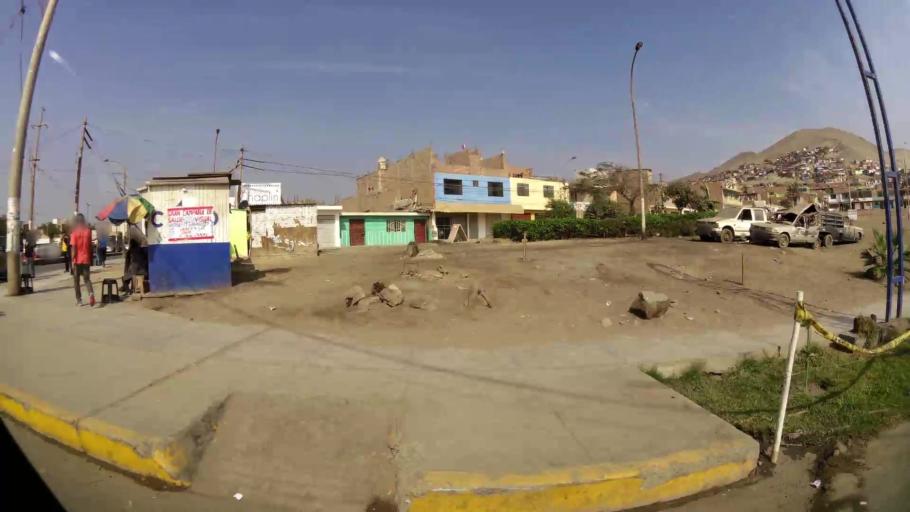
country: PE
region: Lima
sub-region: Lima
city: Santa Rosa
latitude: -11.7763
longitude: -77.1698
